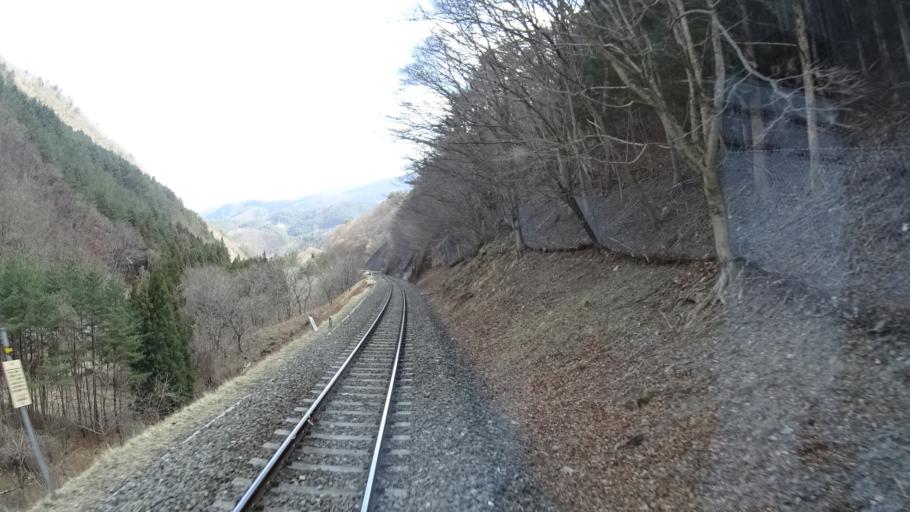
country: JP
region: Iwate
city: Kamaishi
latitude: 39.2585
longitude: 141.7317
